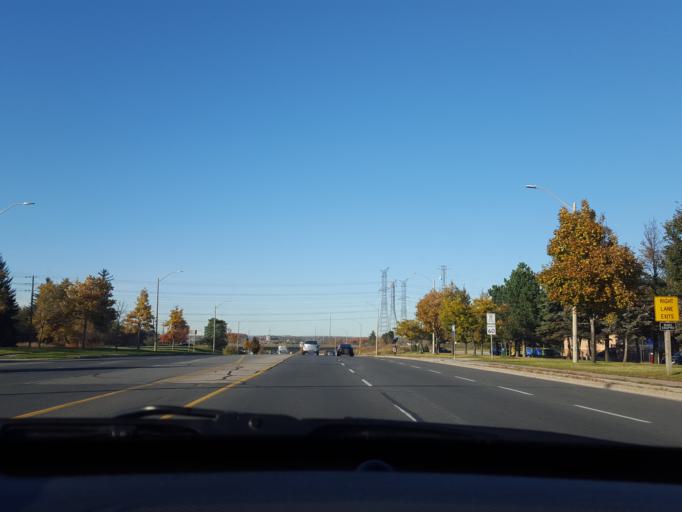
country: CA
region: Ontario
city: Markham
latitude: 43.8498
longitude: -79.2797
